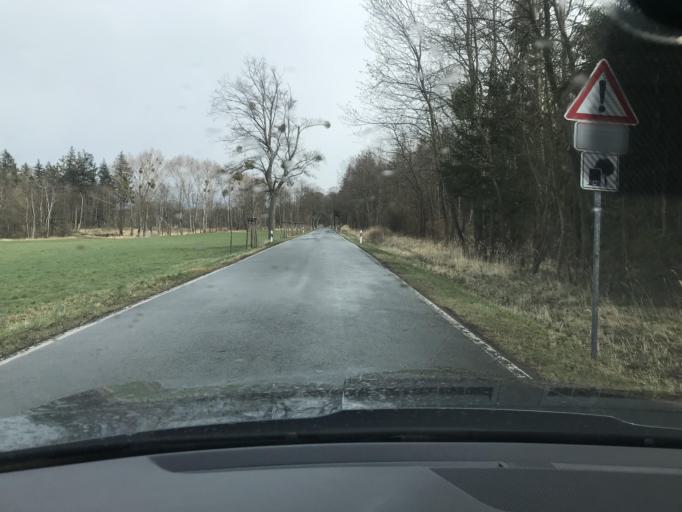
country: DE
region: Saxony-Anhalt
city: Ballenstedt
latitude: 51.6883
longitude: 11.3090
